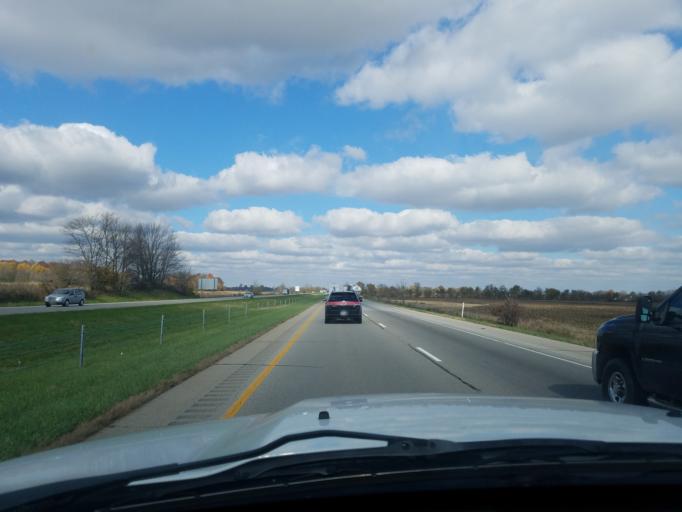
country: US
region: Indiana
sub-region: Bartholomew County
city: Lowell
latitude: 39.2304
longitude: -85.9541
